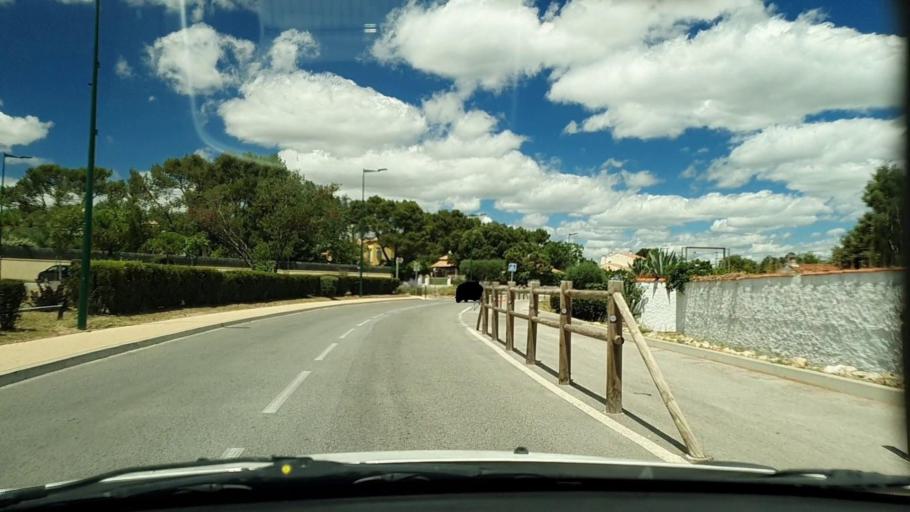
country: FR
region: Languedoc-Roussillon
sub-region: Departement du Gard
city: Poulx
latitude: 43.9005
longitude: 4.4211
